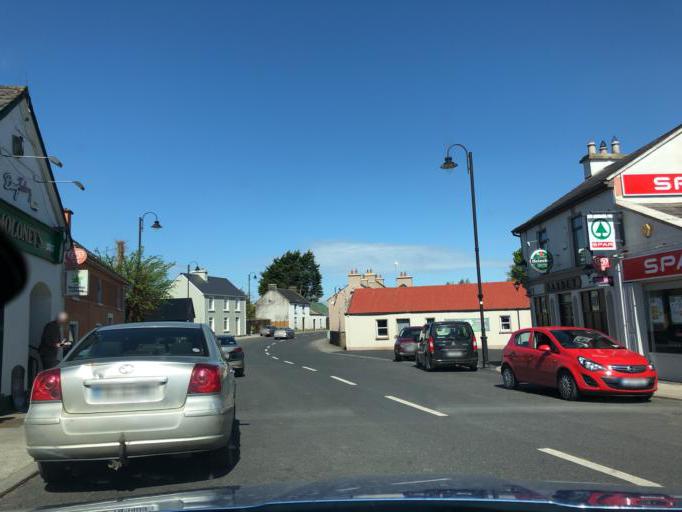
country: IE
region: Connaught
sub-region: County Galway
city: Portumna
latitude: 53.1498
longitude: -8.3733
